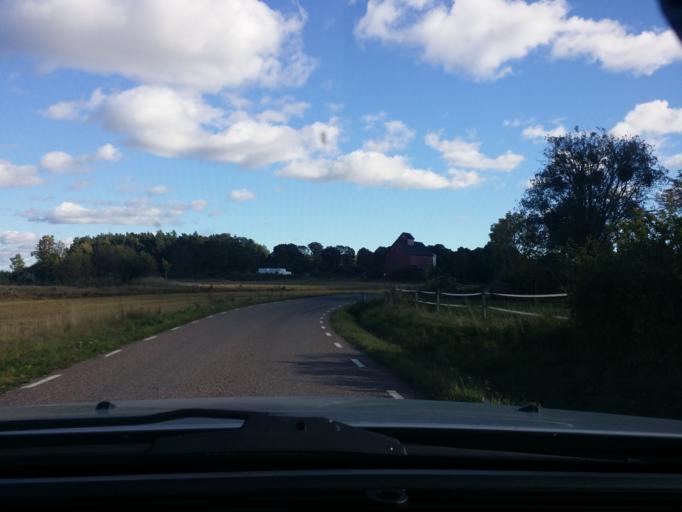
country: SE
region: Vaestmanland
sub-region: Vasteras
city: Vasteras
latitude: 59.5382
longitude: 16.4732
